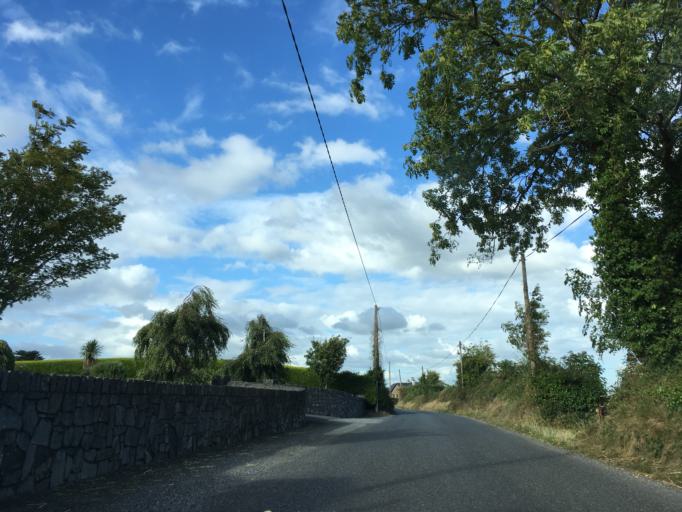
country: IE
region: Munster
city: Cahir
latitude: 52.2884
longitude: -7.9543
